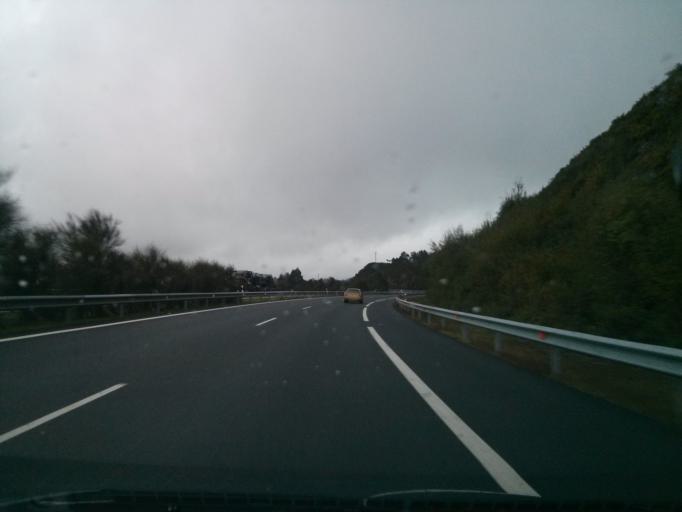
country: ES
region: Galicia
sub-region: Provincia de Ourense
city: Melon
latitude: 42.2283
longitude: -8.2363
